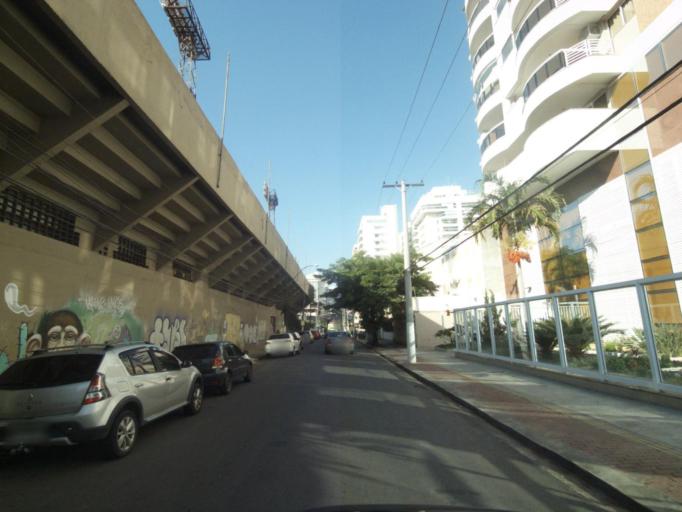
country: BR
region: Rio de Janeiro
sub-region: Niteroi
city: Niteroi
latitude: -22.9011
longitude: -43.1056
